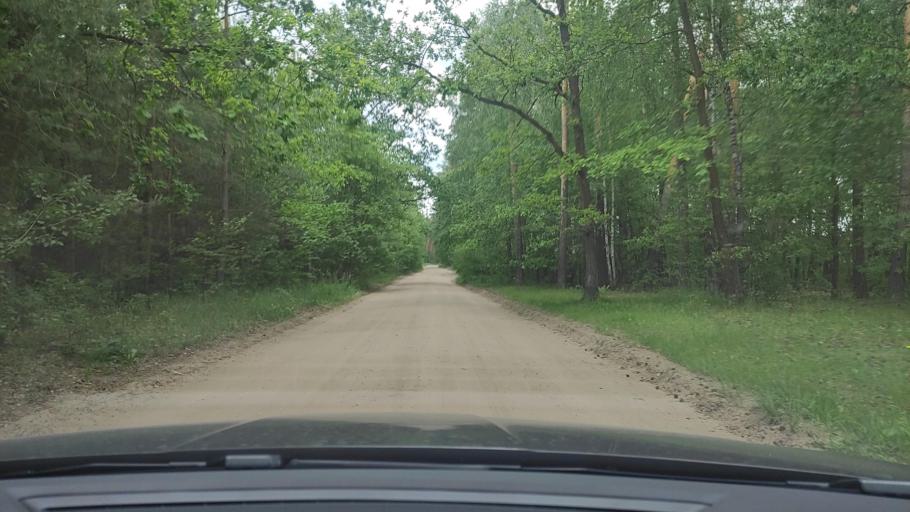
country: PL
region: Greater Poland Voivodeship
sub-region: Powiat poznanski
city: Pobiedziska
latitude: 52.4947
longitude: 17.2004
